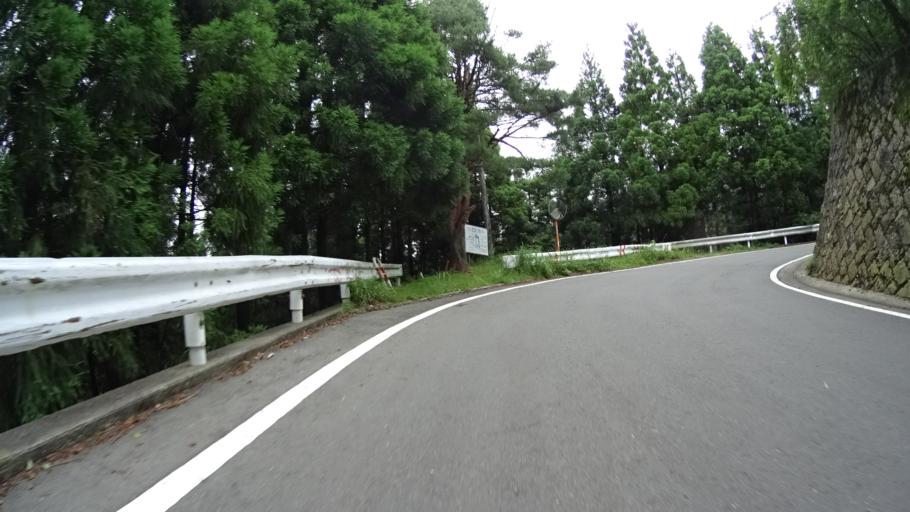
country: JP
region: Kanagawa
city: Hadano
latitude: 35.4325
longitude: 139.2124
